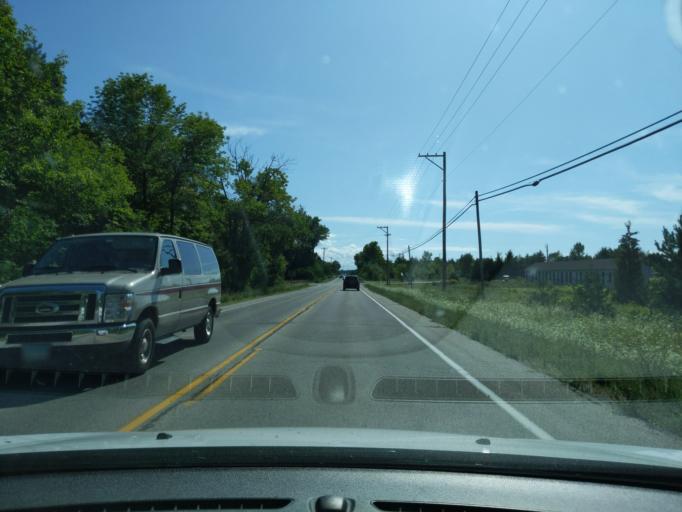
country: US
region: Wisconsin
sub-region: Door County
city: Sturgeon Bay
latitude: 45.2158
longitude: -87.1110
